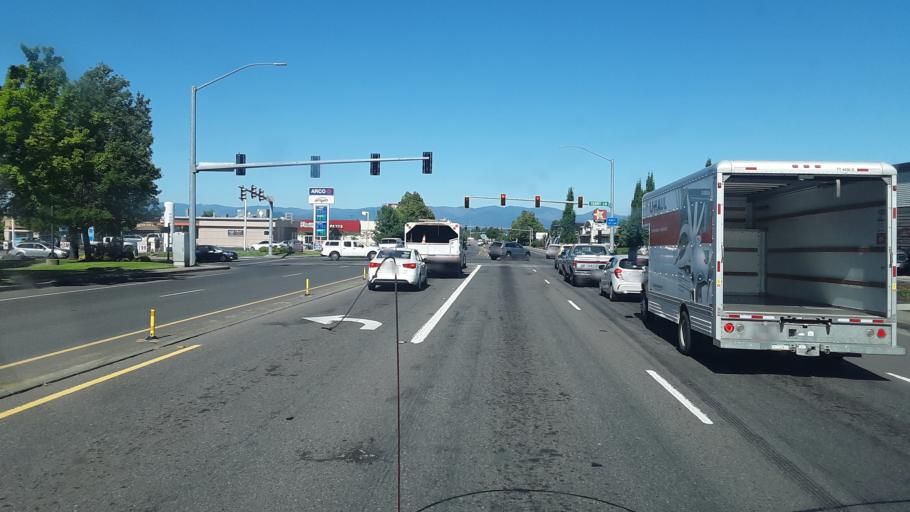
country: US
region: Oregon
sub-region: Josephine County
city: Fruitdale
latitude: 42.4367
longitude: -123.3020
